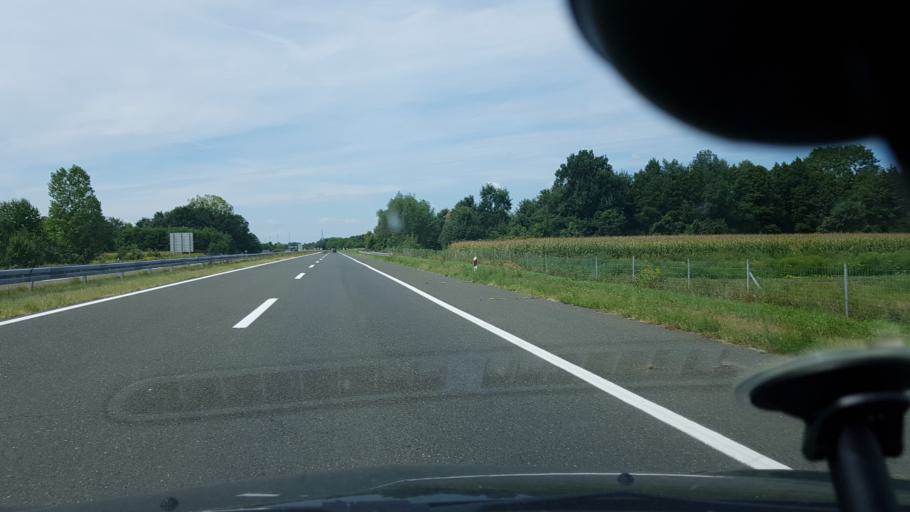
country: HR
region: Medimurska
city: Hodosan
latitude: 46.4108
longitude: 16.6561
